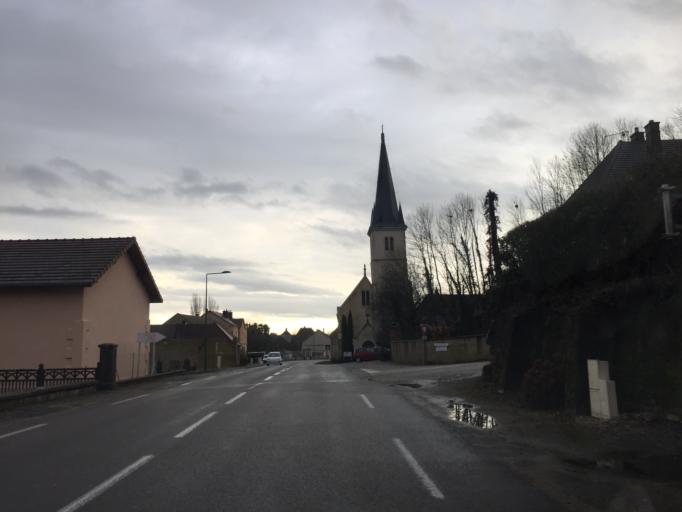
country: FR
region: Franche-Comte
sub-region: Departement du Jura
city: Mont-sous-Vaudrey
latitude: 46.9945
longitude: 5.5505
